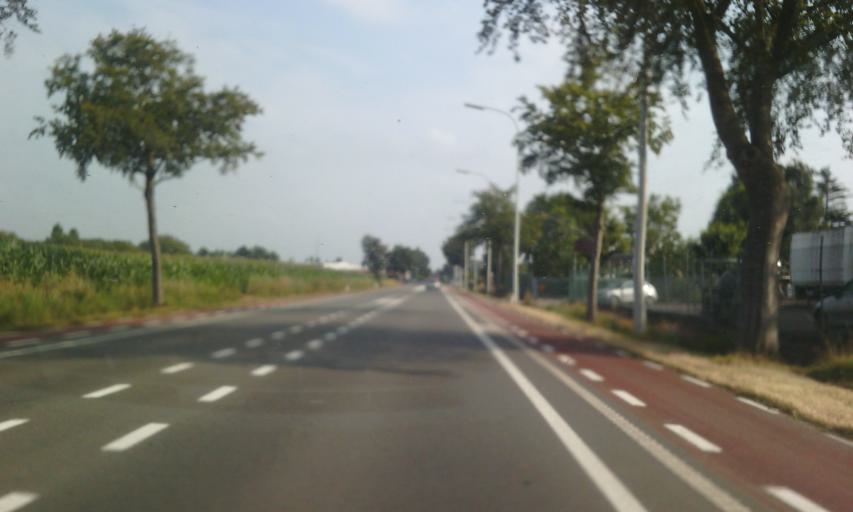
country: BE
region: Flanders
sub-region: Provincie Oost-Vlaanderen
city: Waarschoot
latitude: 51.1314
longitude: 3.6064
